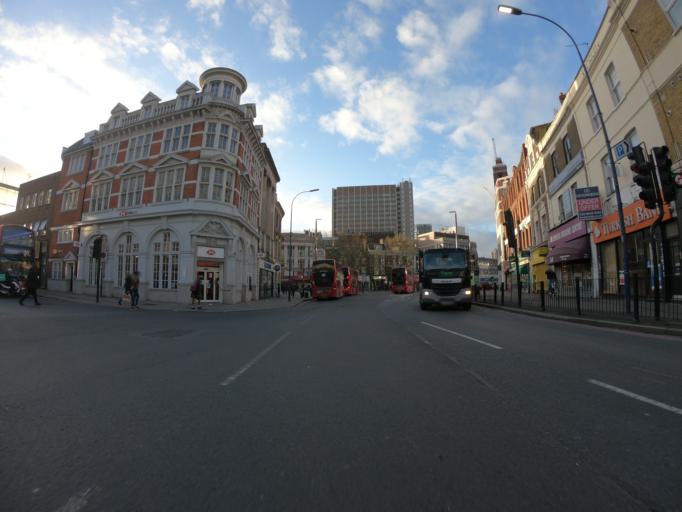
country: GB
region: England
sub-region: Greater London
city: Blackheath
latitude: 51.4624
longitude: -0.0092
